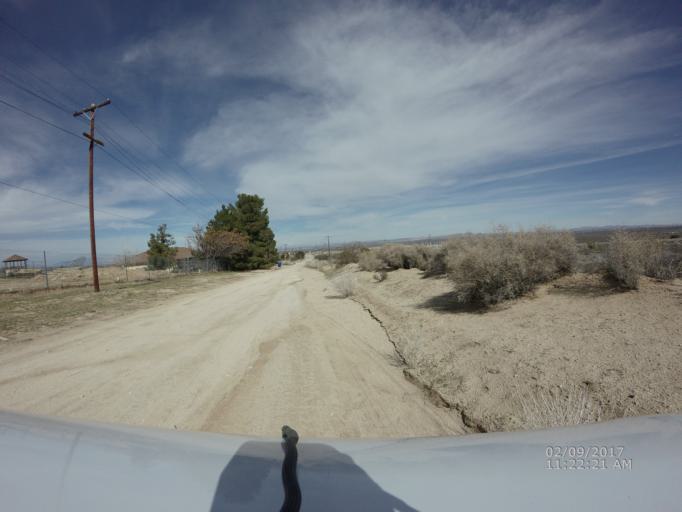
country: US
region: California
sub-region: Los Angeles County
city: Littlerock
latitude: 34.5035
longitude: -117.9229
